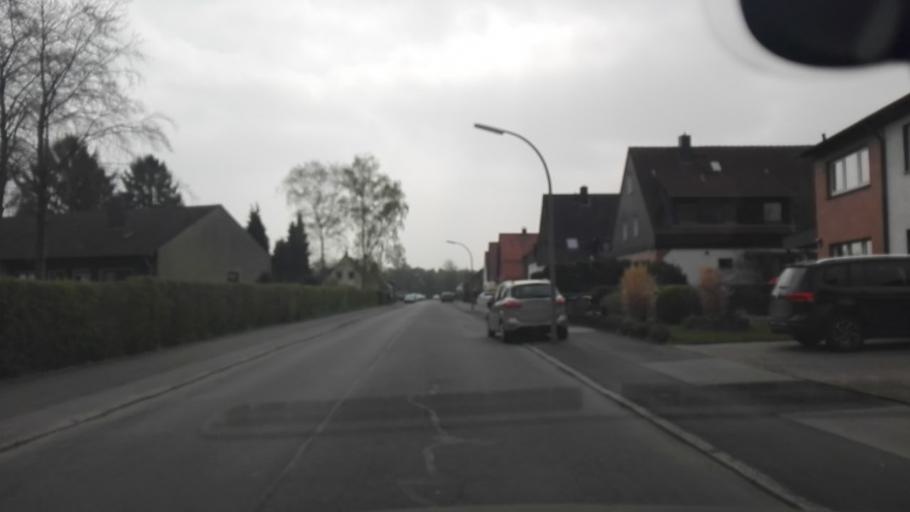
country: DE
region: North Rhine-Westphalia
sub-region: Regierungsbezirk Arnsberg
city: Dortmund
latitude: 51.4733
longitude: 7.4201
